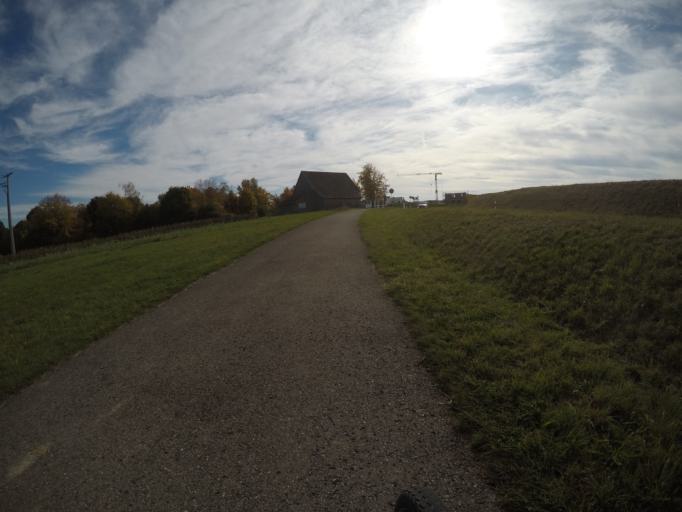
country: DE
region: Baden-Wuerttemberg
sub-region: Regierungsbezirk Stuttgart
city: Gartringen
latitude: 48.6462
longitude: 8.8913
